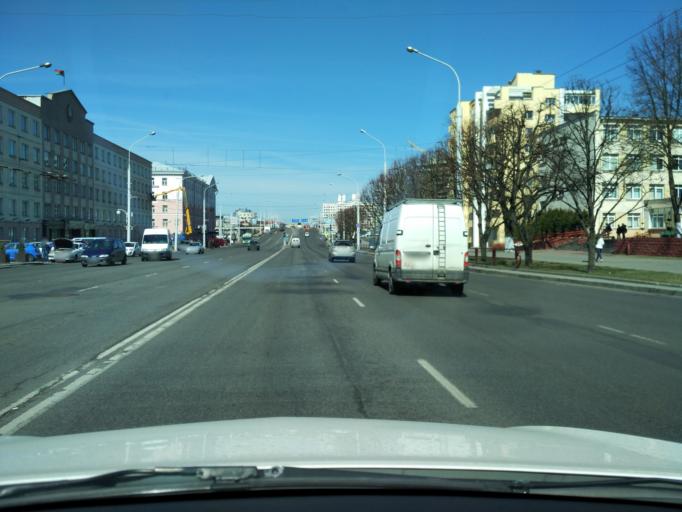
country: BY
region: Minsk
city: Minsk
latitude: 53.8800
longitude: 27.5354
